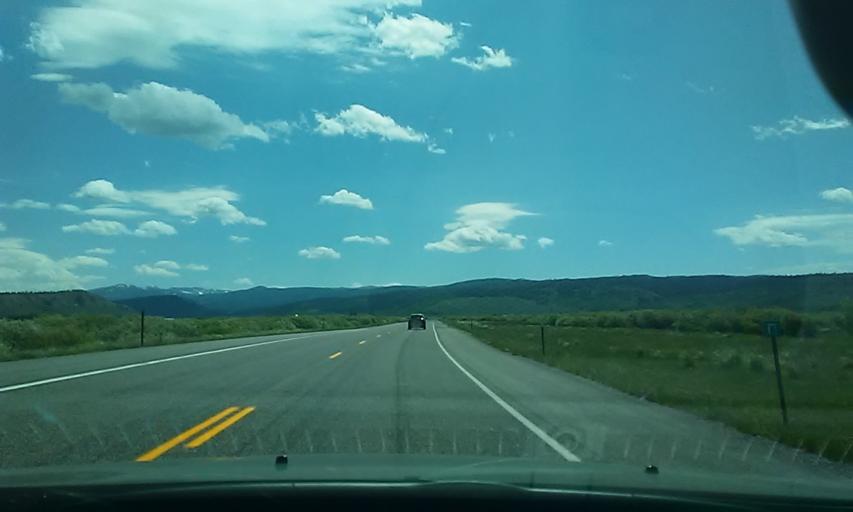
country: US
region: Wyoming
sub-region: Teton County
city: Jackson
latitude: 43.8377
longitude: -110.4373
